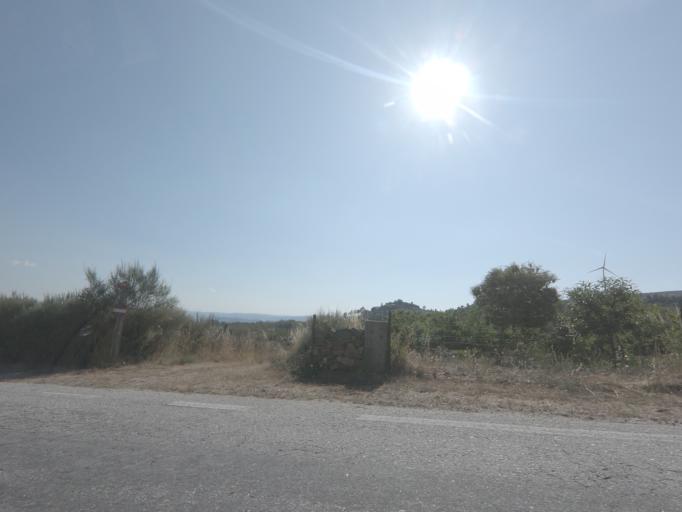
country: PT
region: Viseu
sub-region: Tabuaco
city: Tabuaco
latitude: 41.0607
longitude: -7.5620
